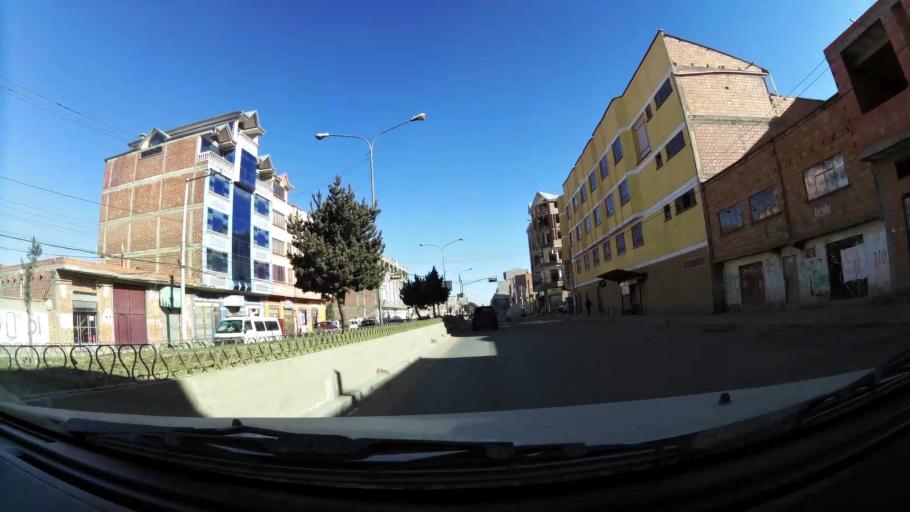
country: BO
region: La Paz
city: La Paz
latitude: -16.5409
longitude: -68.1818
